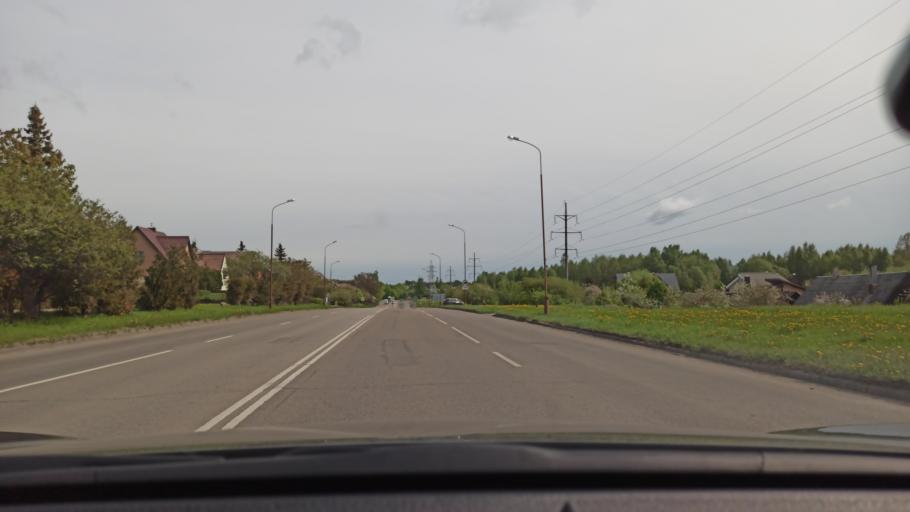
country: LT
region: Siauliu apskritis
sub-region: Siauliai
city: Siauliai
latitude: 55.9192
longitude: 23.3457
